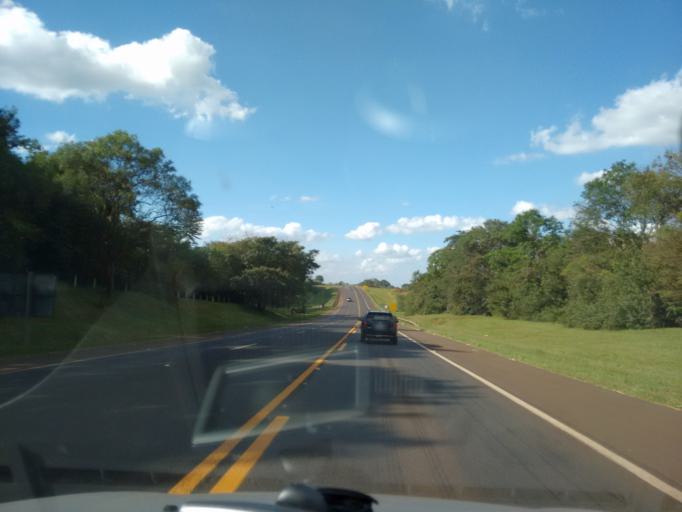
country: BR
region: Sao Paulo
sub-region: Americo Brasiliense
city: Americo Brasiliense
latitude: -21.7583
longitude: -48.0733
